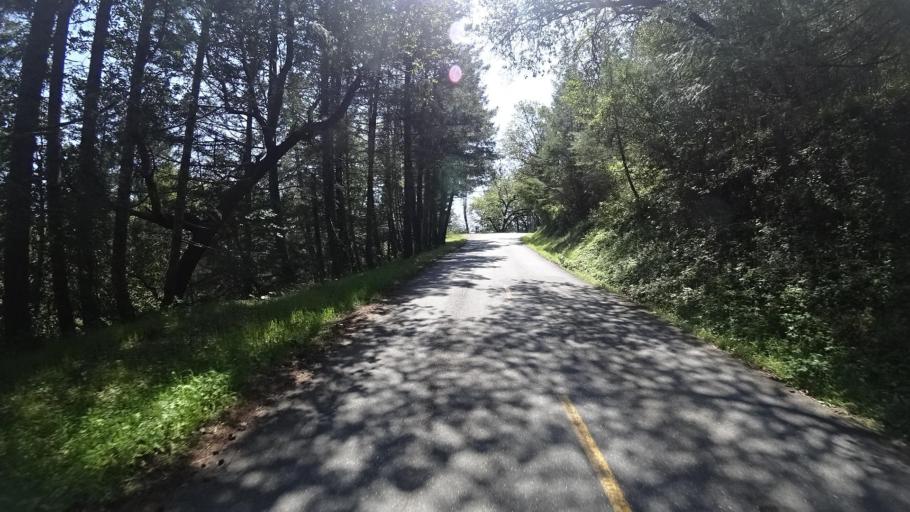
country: US
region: California
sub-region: Humboldt County
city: Redway
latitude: 40.1607
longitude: -123.6156
